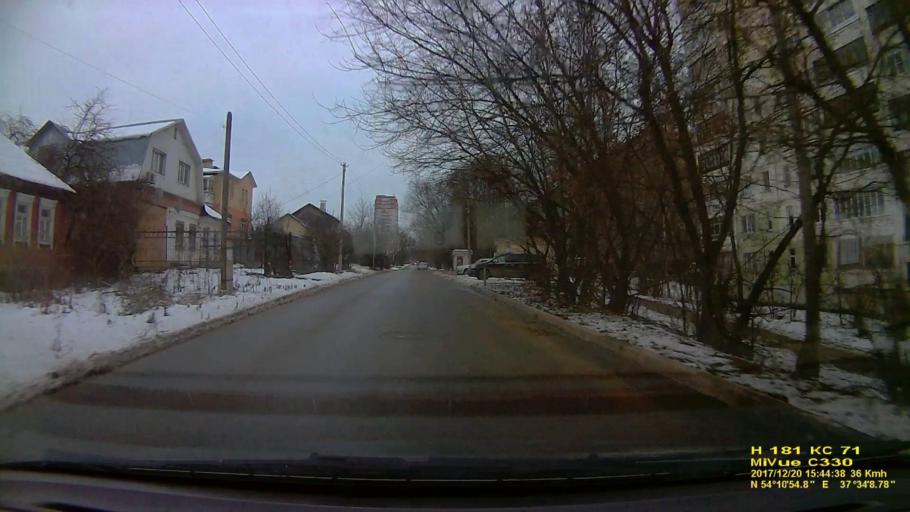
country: RU
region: Tula
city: Mendeleyevskiy
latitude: 54.1818
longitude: 37.5692
